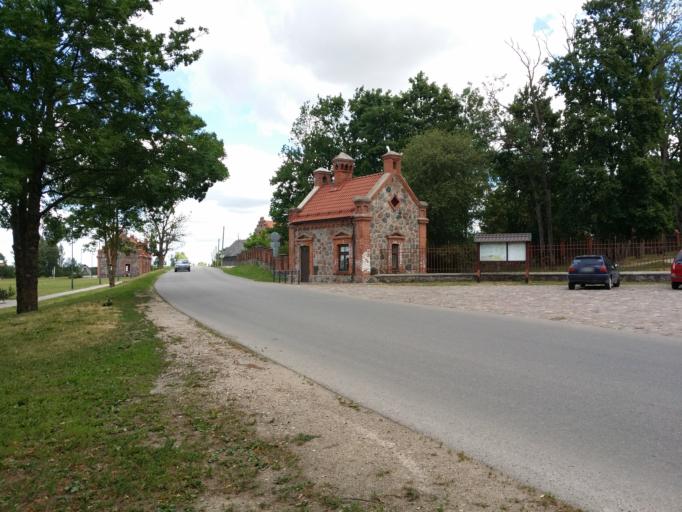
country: LT
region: Panevezys
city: Rokiskis
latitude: 55.9650
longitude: 25.5961
